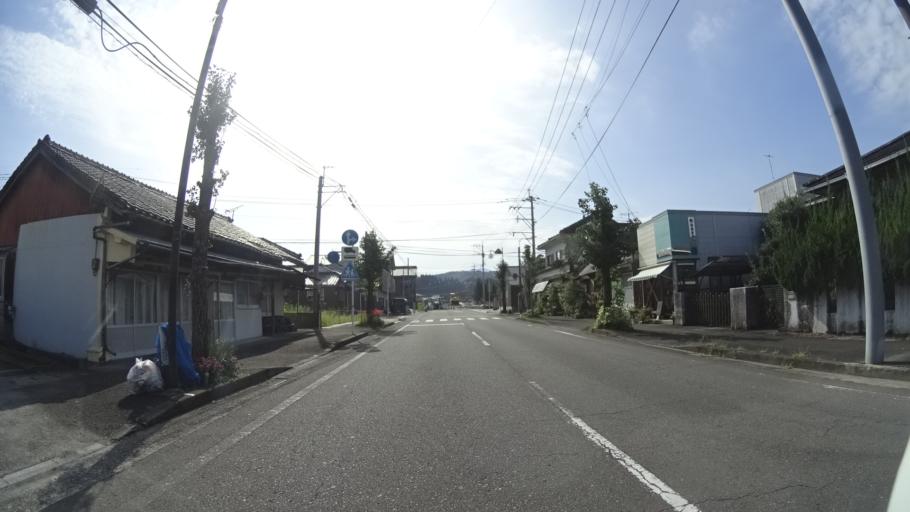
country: JP
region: Kagoshima
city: Okuchi-shinohara
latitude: 32.0461
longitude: 130.7662
